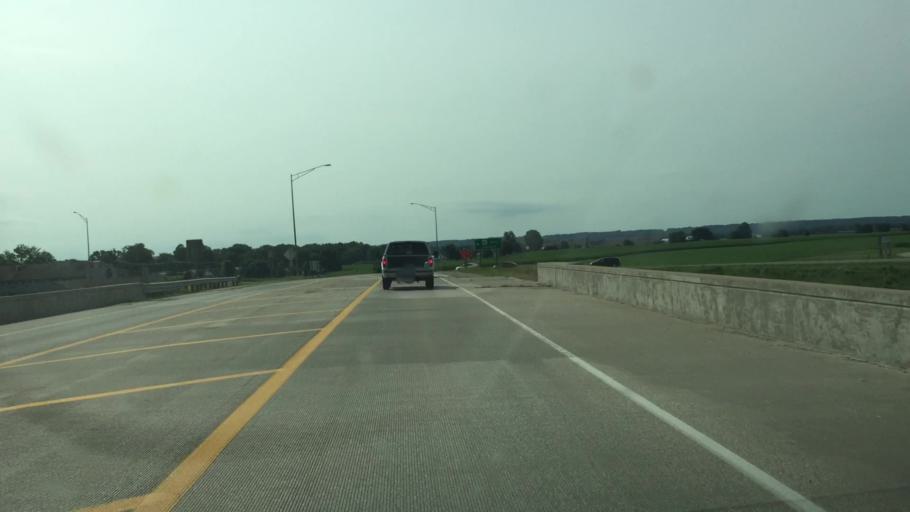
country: US
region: Illinois
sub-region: Hancock County
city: Nauvoo
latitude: 40.6260
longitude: -91.3988
